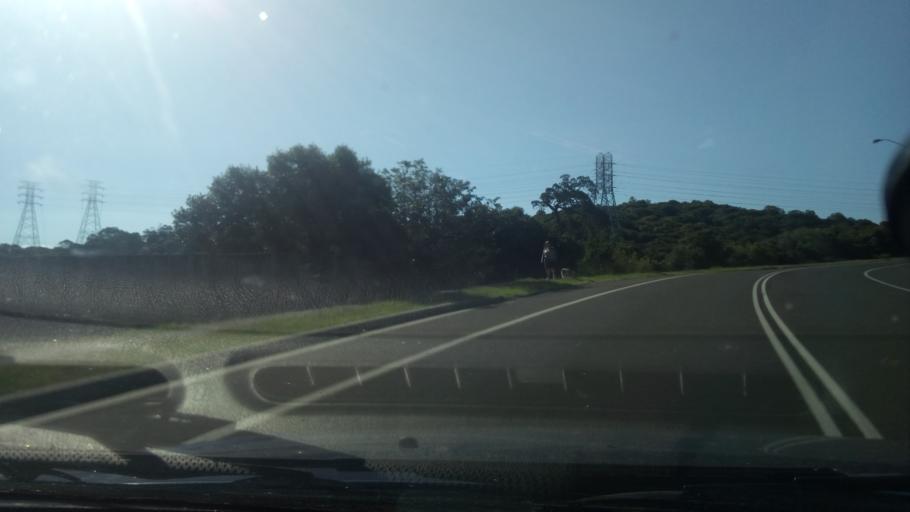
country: AU
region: New South Wales
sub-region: Wollongong
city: Berkeley
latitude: -34.4720
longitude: 150.8528
